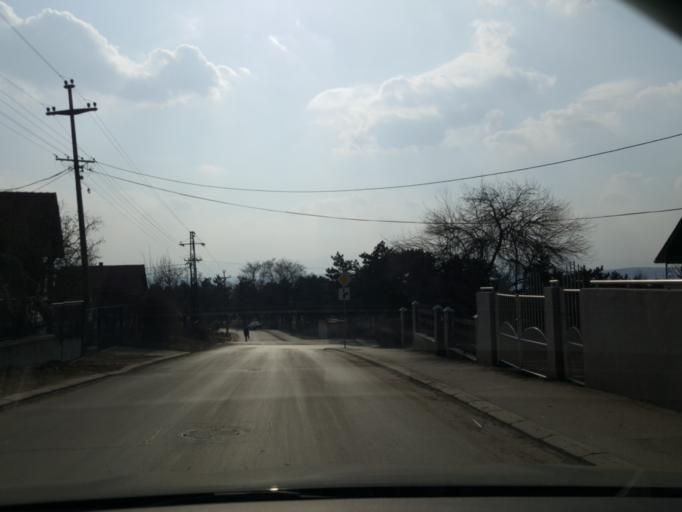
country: RS
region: Central Serbia
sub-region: Nisavski Okrug
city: Aleksinac
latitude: 43.5336
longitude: 21.7148
